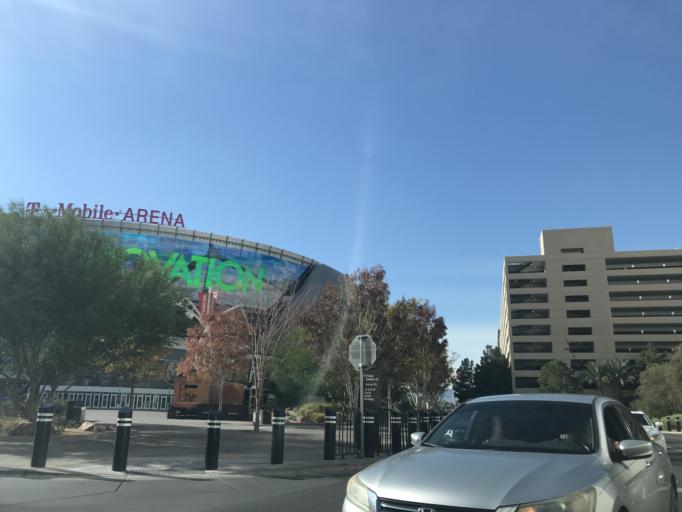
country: US
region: Nevada
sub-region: Clark County
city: Paradise
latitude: 36.1039
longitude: -115.1763
